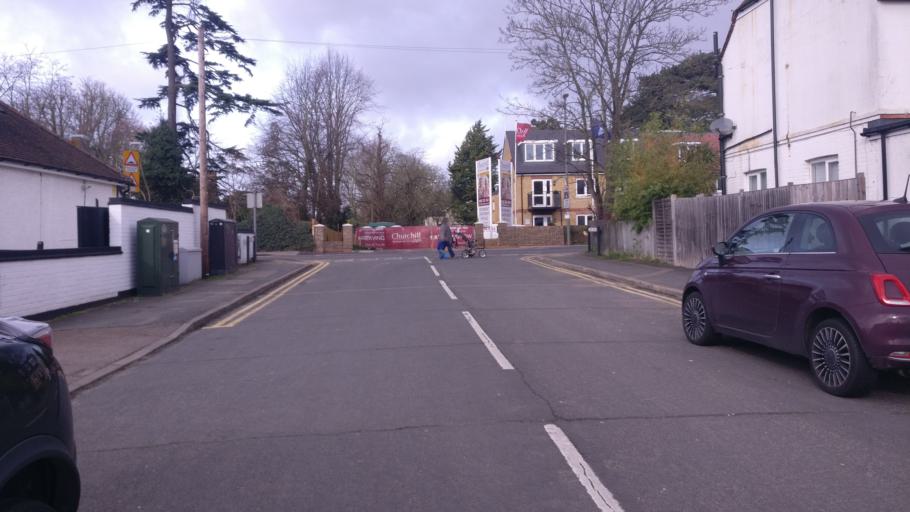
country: GB
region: England
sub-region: Surrey
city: Staines
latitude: 51.4303
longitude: -0.5202
